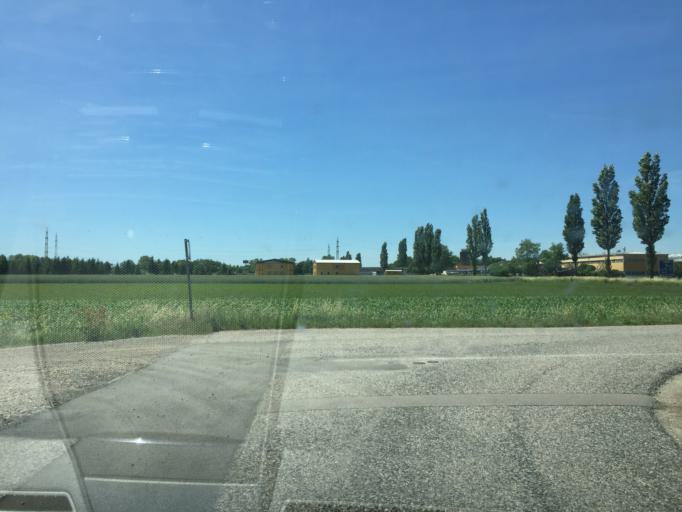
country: AT
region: Lower Austria
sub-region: Politischer Bezirk Sankt Polten
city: Herzogenburg
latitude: 48.2329
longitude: 15.6867
